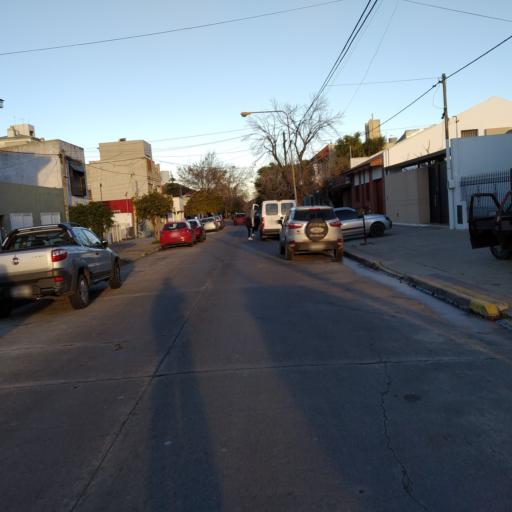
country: AR
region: Buenos Aires
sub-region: Partido de La Plata
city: La Plata
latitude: -34.9450
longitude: -57.9594
